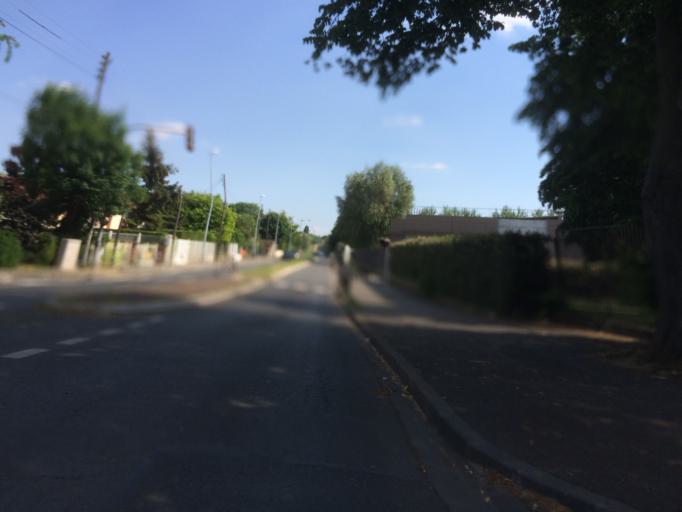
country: FR
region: Ile-de-France
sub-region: Departement de l'Essonne
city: Savigny-sur-Orge
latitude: 48.6784
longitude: 2.3595
